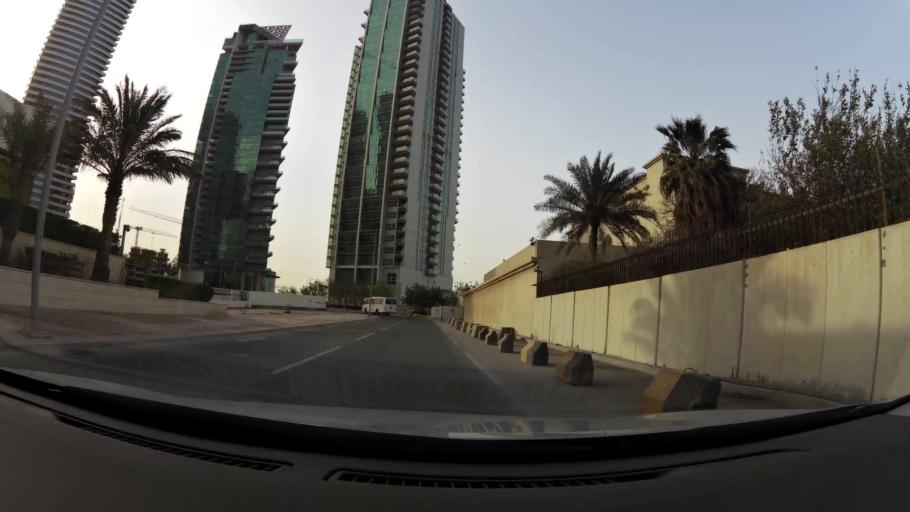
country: QA
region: Baladiyat ad Dawhah
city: Doha
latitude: 25.3298
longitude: 51.5361
